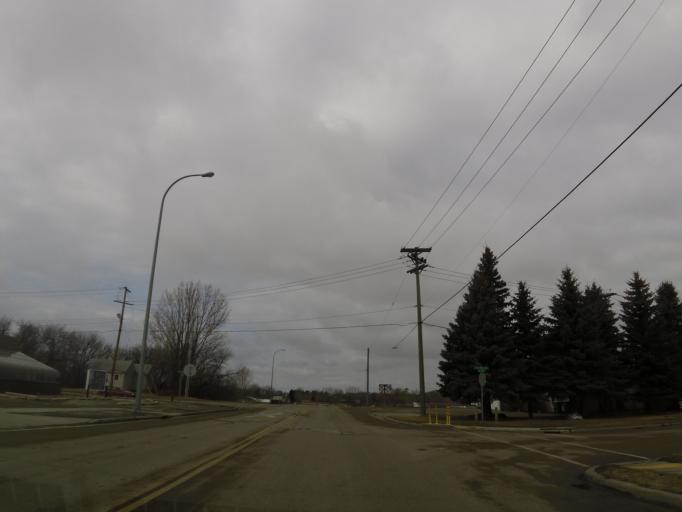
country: US
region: North Dakota
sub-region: Traill County
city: Mayville
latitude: 47.4981
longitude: -97.3235
